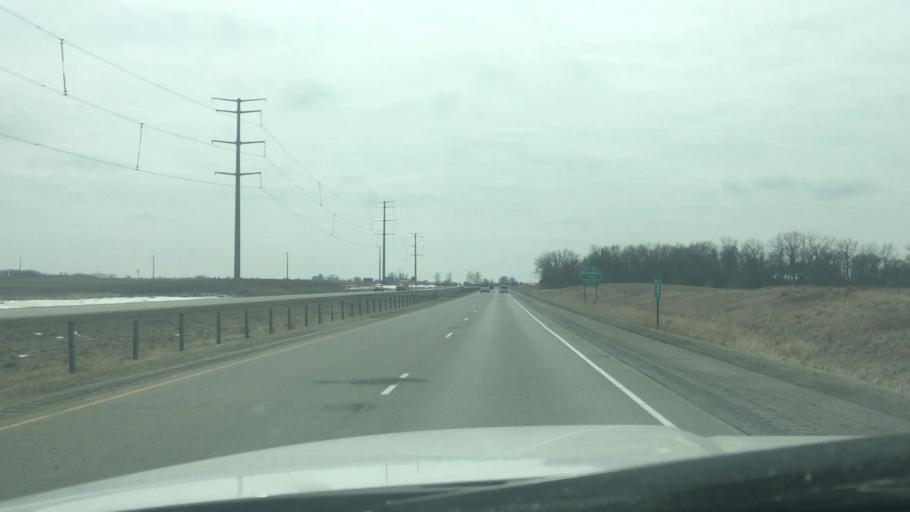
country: US
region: Minnesota
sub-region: Clay County
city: Barnesville
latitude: 46.4982
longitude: -96.2909
